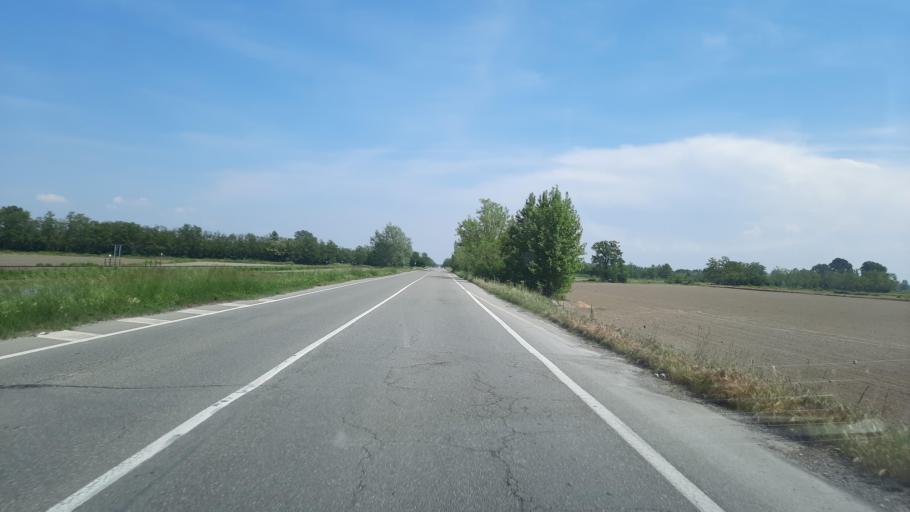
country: IT
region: Lombardy
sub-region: Provincia di Pavia
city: Cergnago
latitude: 45.2323
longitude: 8.8076
